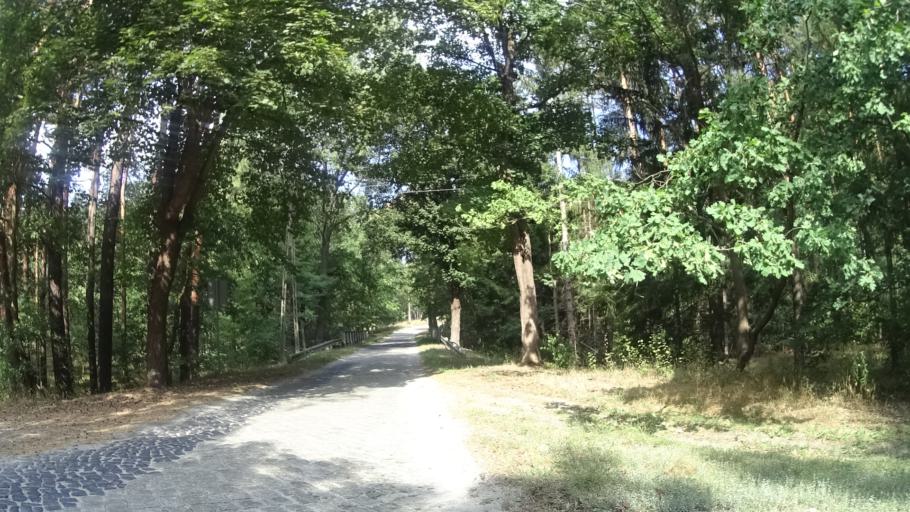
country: PL
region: Lubusz
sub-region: Powiat zarski
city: Leknica
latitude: 51.5249
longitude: 14.8221
